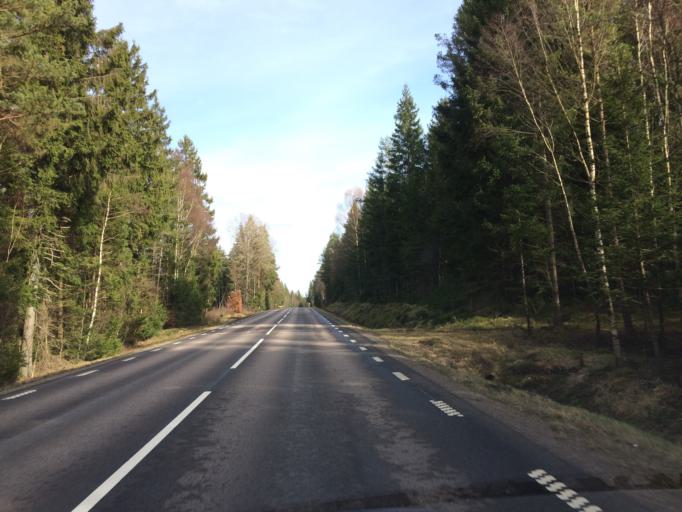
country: SE
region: Halland
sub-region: Hylte Kommun
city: Hyltebruk
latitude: 57.0209
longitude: 13.1831
